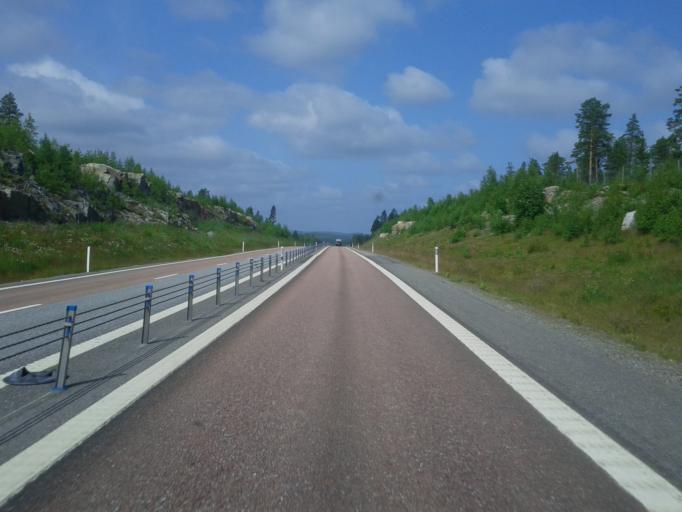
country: SE
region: Vaesterbotten
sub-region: Skelleftea Kommun
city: Soedra Bergsbyn
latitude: 64.6868
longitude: 21.0550
